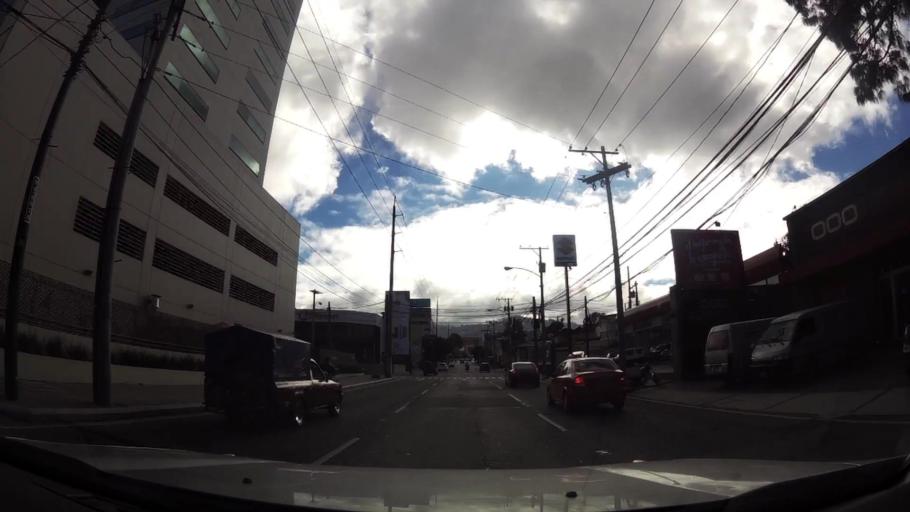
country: GT
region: Guatemala
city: Santa Catarina Pinula
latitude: 14.5877
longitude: -90.5045
